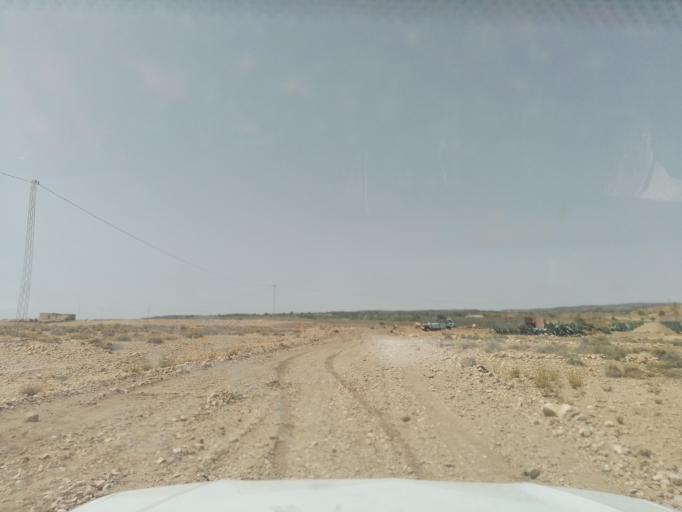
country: TN
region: Al Qasrayn
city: Kasserine
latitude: 35.2866
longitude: 8.9264
